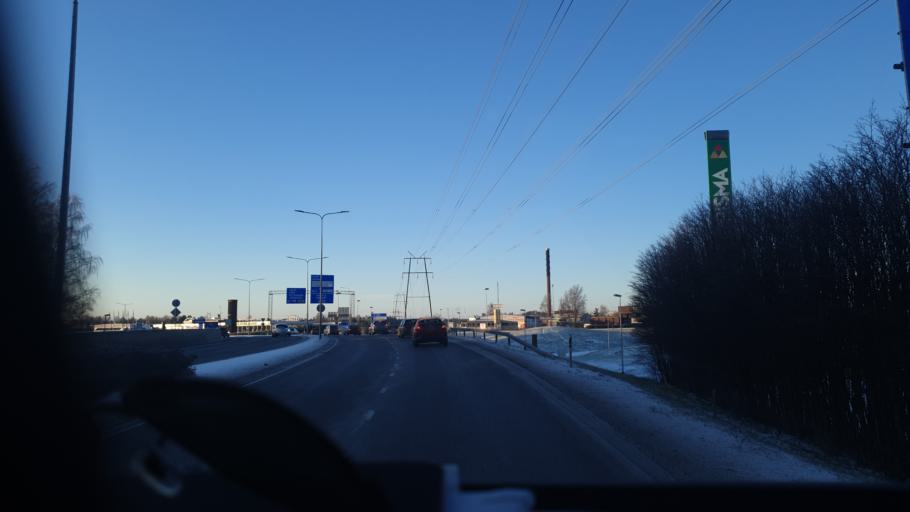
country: FI
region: Central Ostrobothnia
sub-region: Kokkola
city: Kokkola
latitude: 63.8312
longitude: 23.1247
